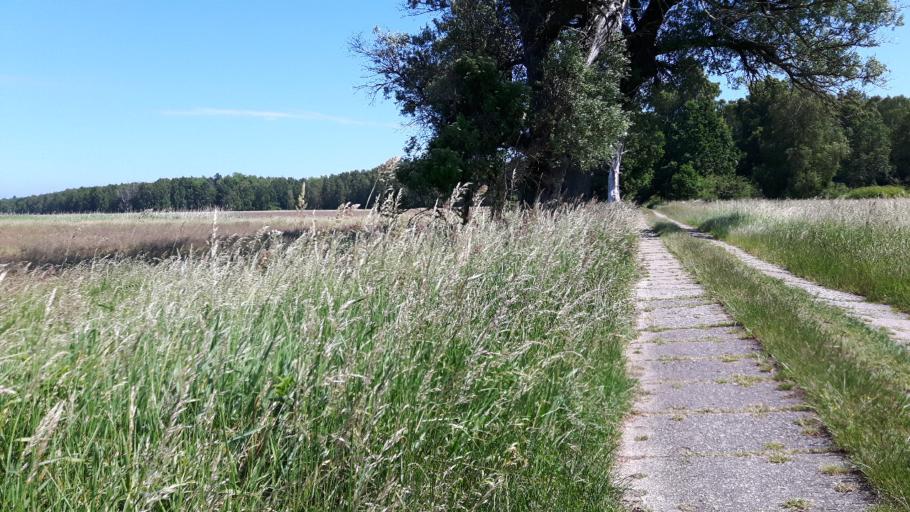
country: PL
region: Pomeranian Voivodeship
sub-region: Powiat slupski
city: Smoldzino
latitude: 54.6704
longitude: 17.1686
